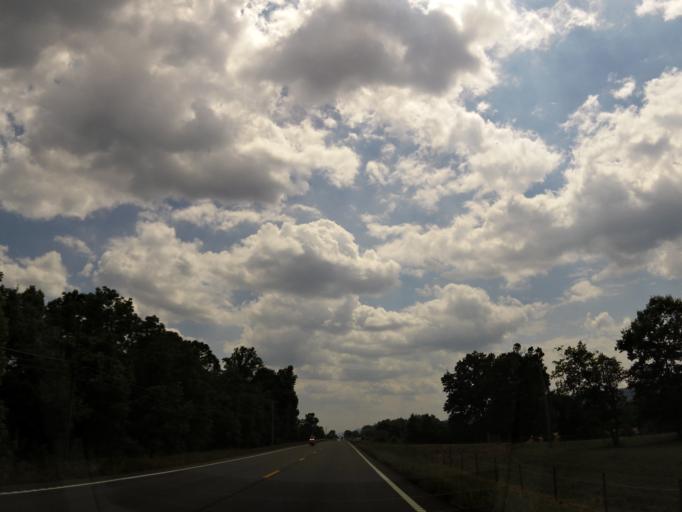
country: US
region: Tennessee
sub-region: Sequatchie County
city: Dunlap
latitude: 35.4935
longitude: -85.2993
